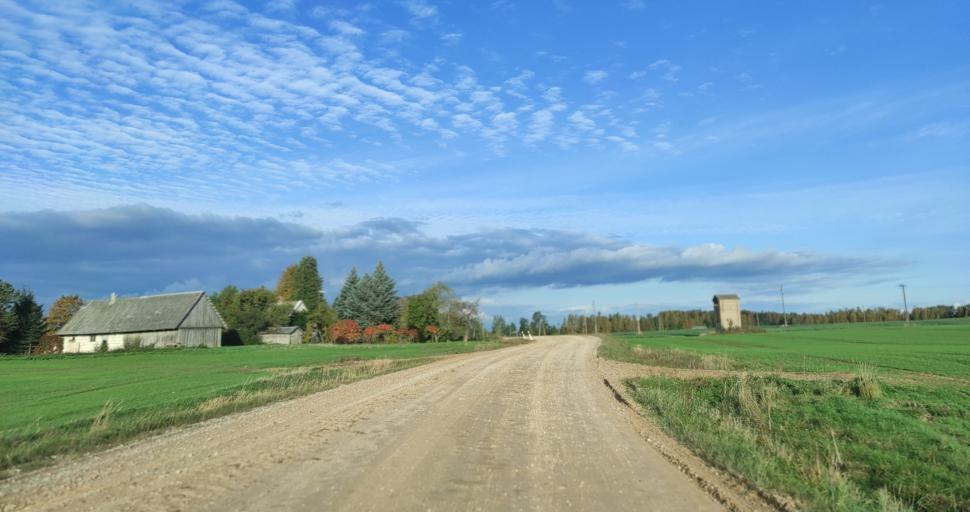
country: LV
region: Skrunda
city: Skrunda
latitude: 56.7453
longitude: 21.8371
